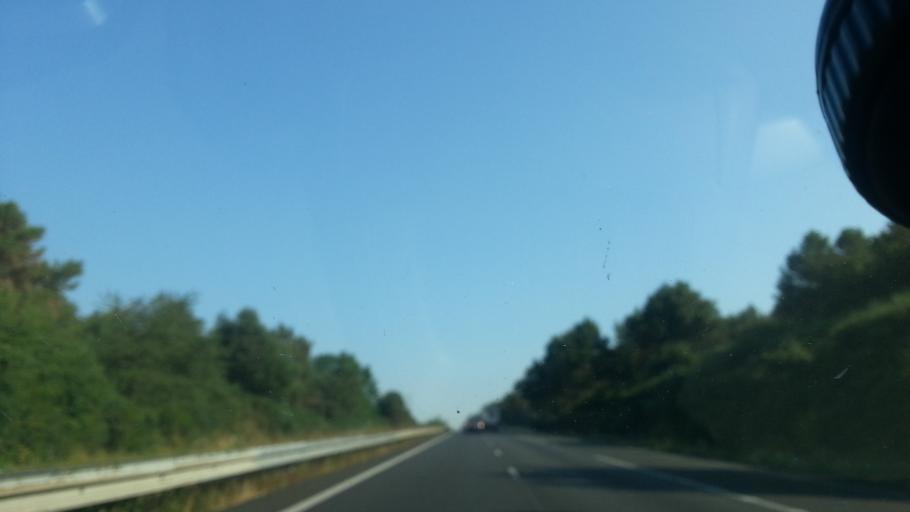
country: FR
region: Poitou-Charentes
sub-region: Departement de la Vienne
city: Dange-Saint-Romain
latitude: 46.9587
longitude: 0.5493
